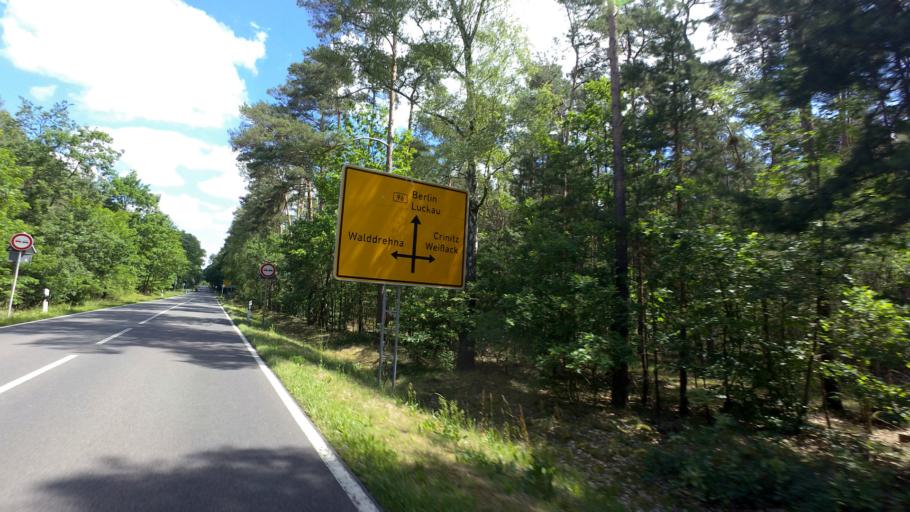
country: DE
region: Brandenburg
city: Sonnewalde
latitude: 51.7553
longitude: 13.6802
